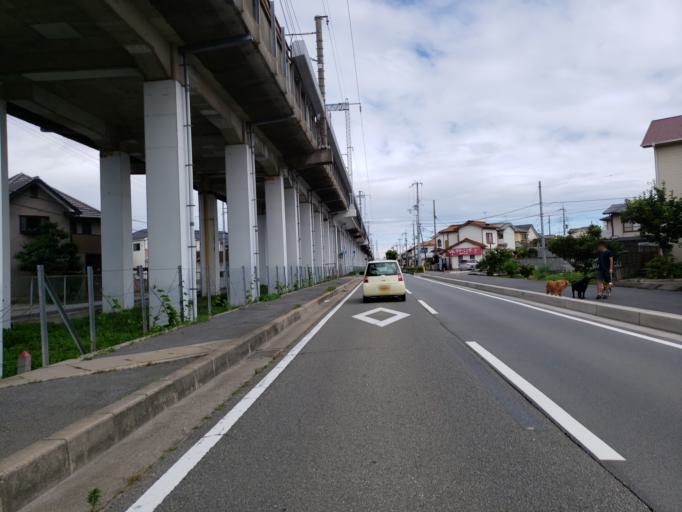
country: JP
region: Hyogo
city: Kakogawacho-honmachi
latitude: 34.7688
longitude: 134.7966
